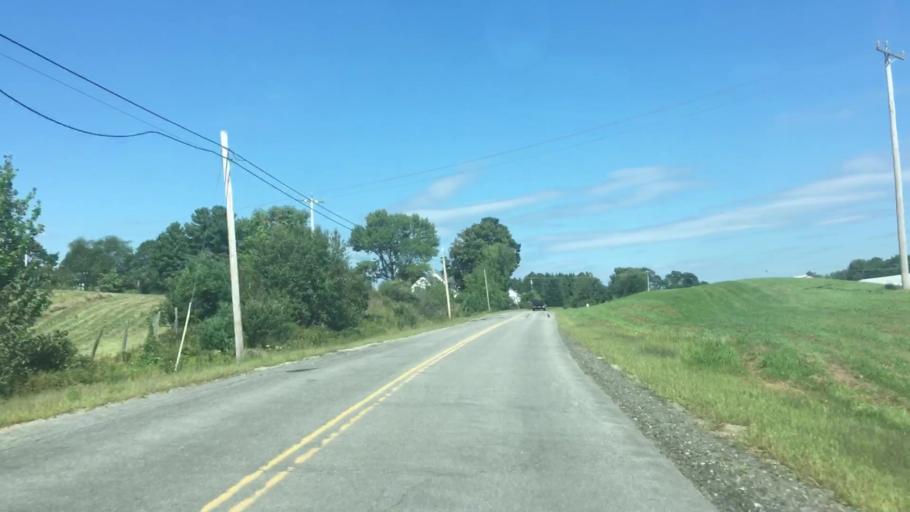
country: US
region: Maine
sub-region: Androscoggin County
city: Lisbon
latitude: 44.0737
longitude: -70.1162
